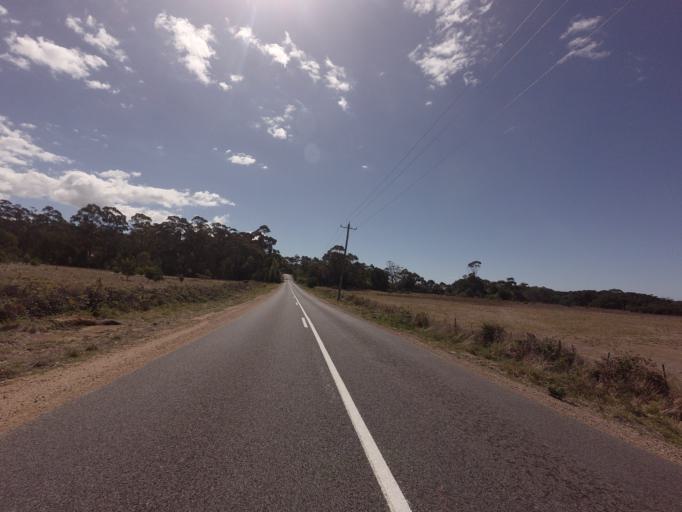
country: AU
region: Tasmania
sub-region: Break O'Day
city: St Helens
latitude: -41.6862
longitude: 148.2812
